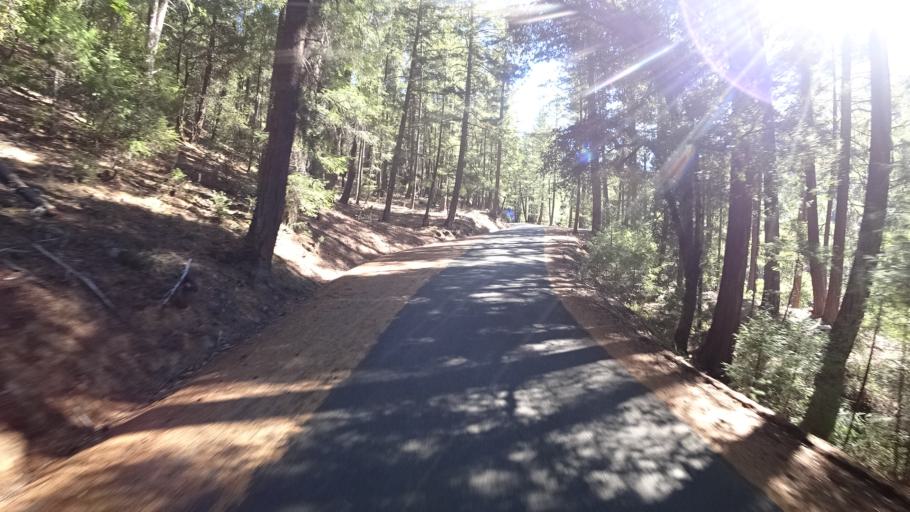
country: US
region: California
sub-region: Siskiyou County
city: Happy Camp
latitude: 41.2992
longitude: -123.1195
